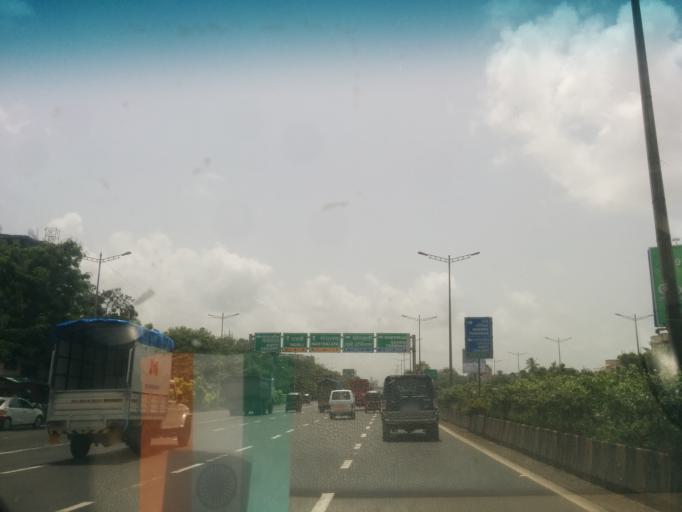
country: IN
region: Maharashtra
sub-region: Mumbai Suburban
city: Mumbai
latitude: 19.0669
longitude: 72.8466
